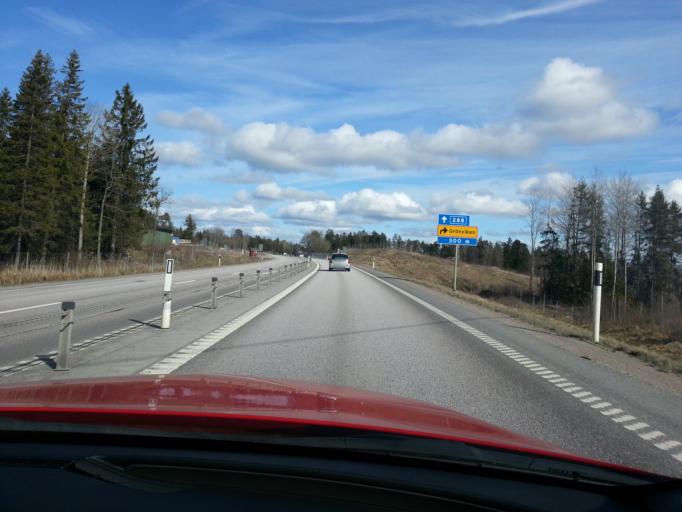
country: SE
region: Uppsala
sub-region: Uppsala Kommun
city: Storvreta
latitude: 59.9176
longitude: 17.7558
